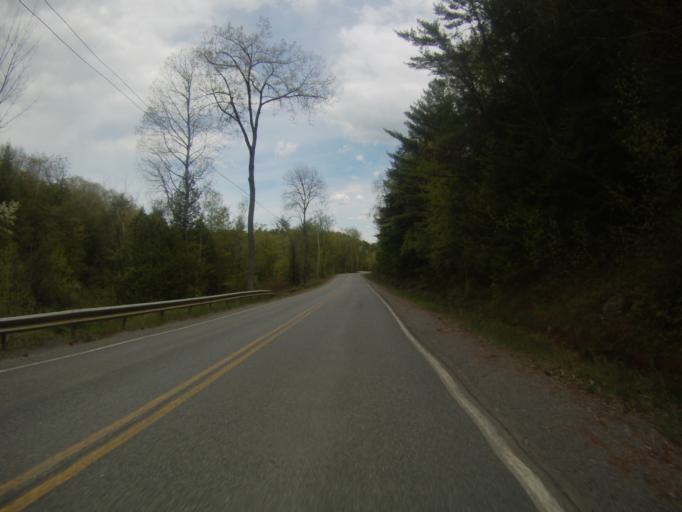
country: US
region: New York
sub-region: Essex County
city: Port Henry
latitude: 43.9463
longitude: -73.4914
